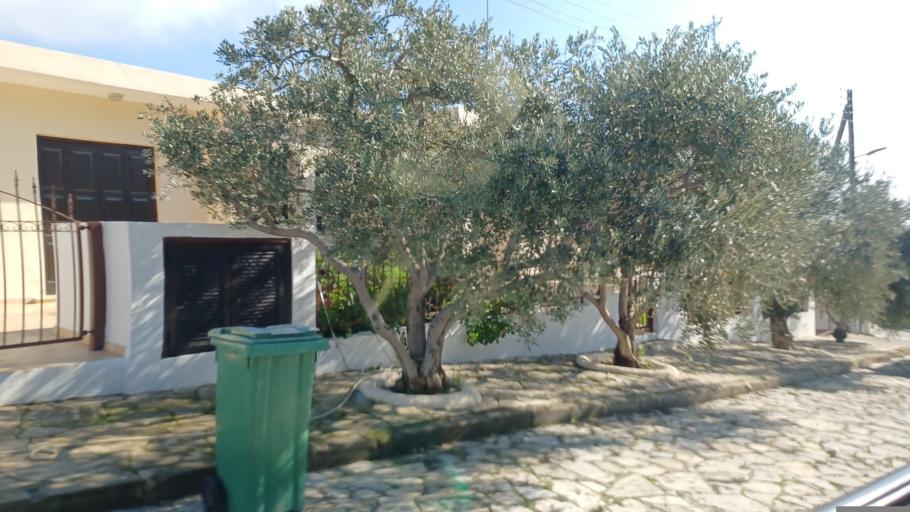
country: CY
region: Larnaka
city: Kofinou
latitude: 34.8529
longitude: 33.3026
